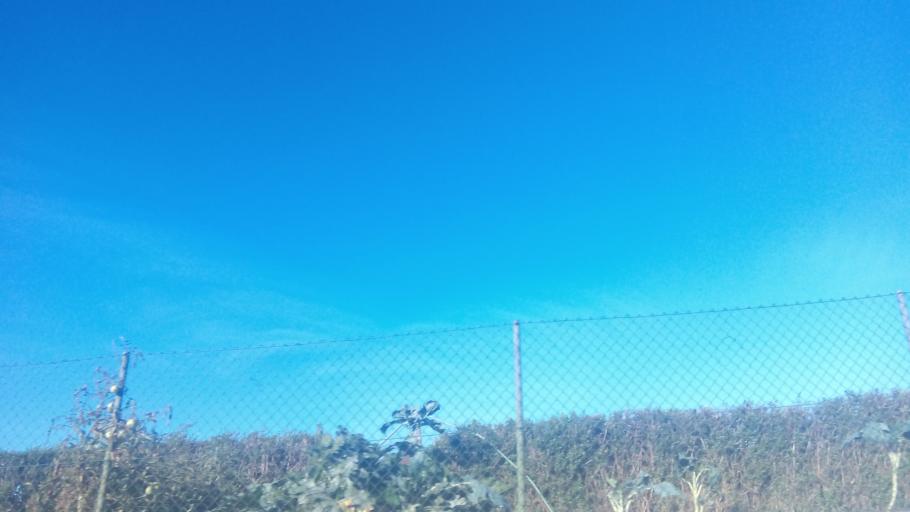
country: PT
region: Porto
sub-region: Paredes
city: Casteloes de Cepeda
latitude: 41.1944
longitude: -8.3447
